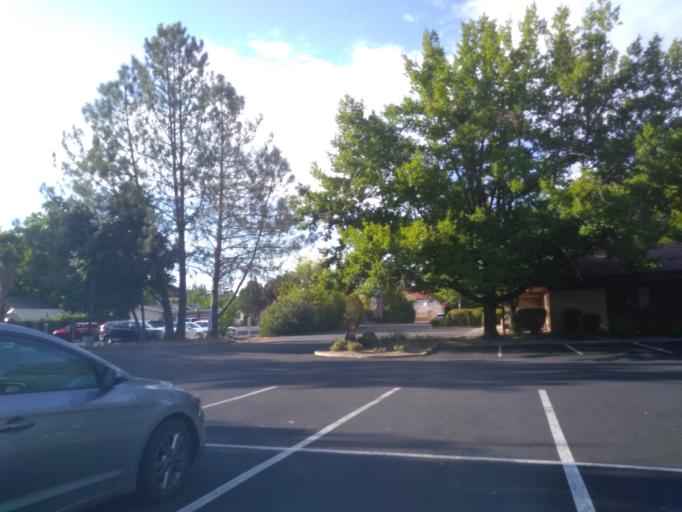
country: US
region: California
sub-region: Mendocino County
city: Ukiah
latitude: 39.1358
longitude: -123.2085
